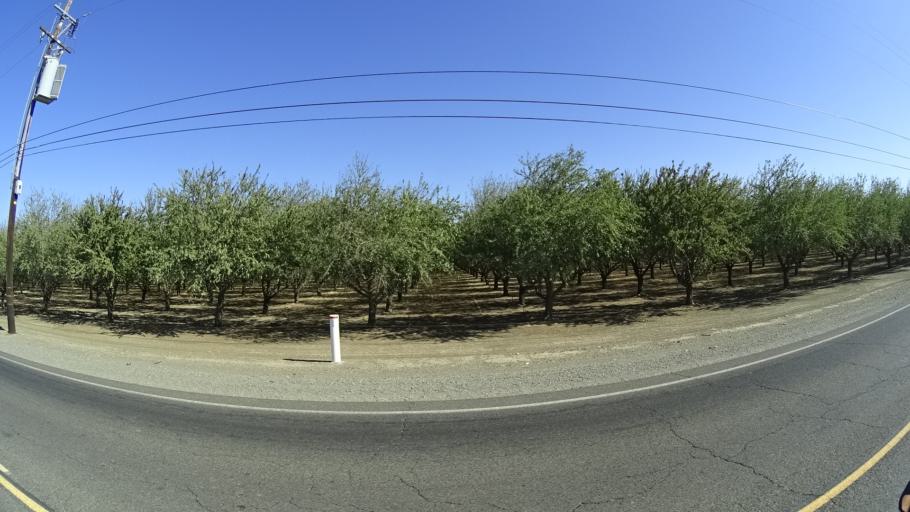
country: US
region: California
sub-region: Yolo County
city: Davis
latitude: 38.5775
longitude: -121.8033
